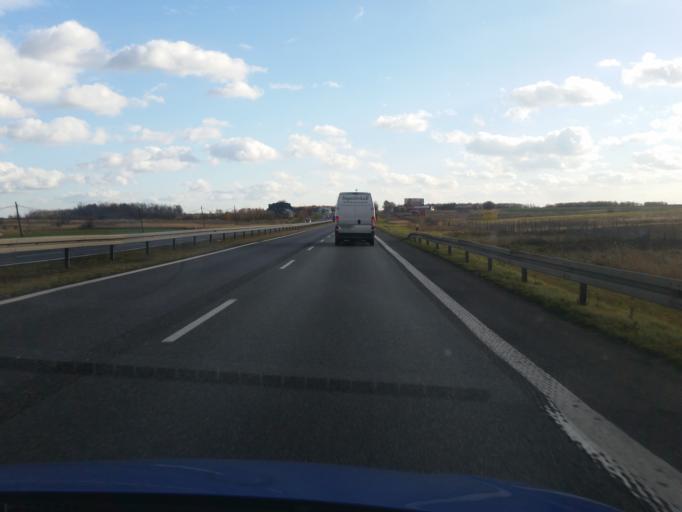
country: PL
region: Silesian Voivodeship
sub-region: Powiat myszkowski
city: Kozieglowy
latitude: 50.6198
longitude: 19.1472
